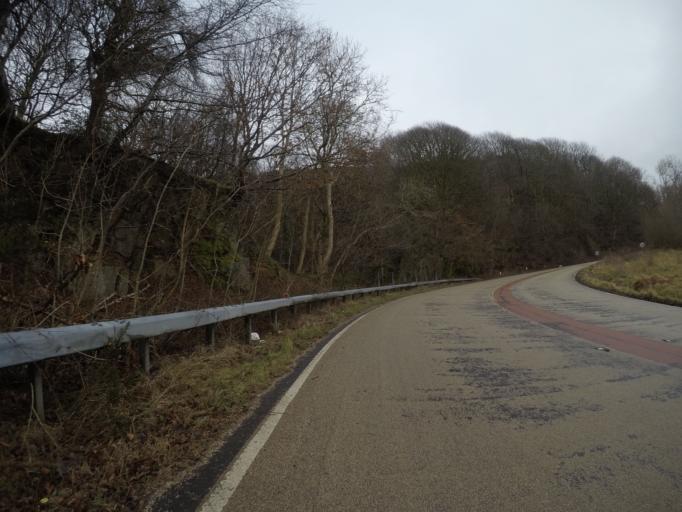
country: GB
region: Scotland
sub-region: North Ayrshire
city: Largs
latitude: 55.7867
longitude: -4.8522
